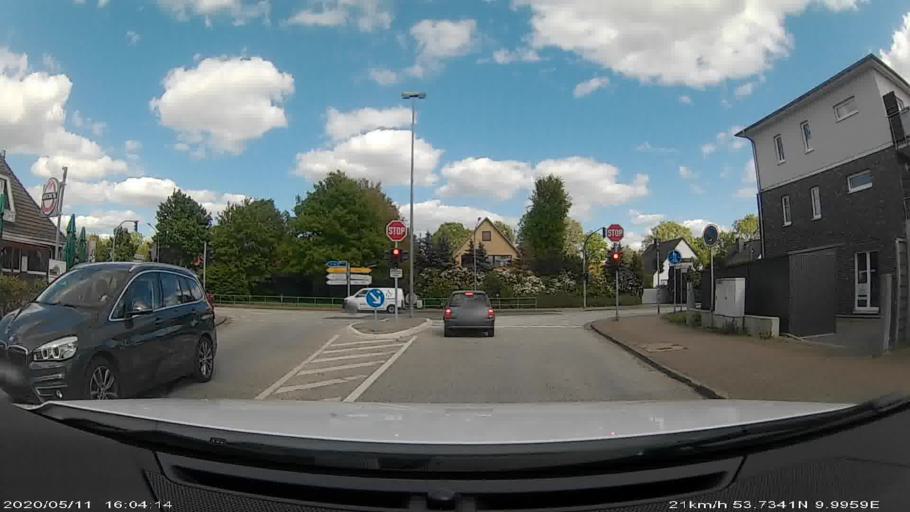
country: DE
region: Schleswig-Holstein
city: Henstedt-Ulzburg
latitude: 53.7417
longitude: 9.9952
